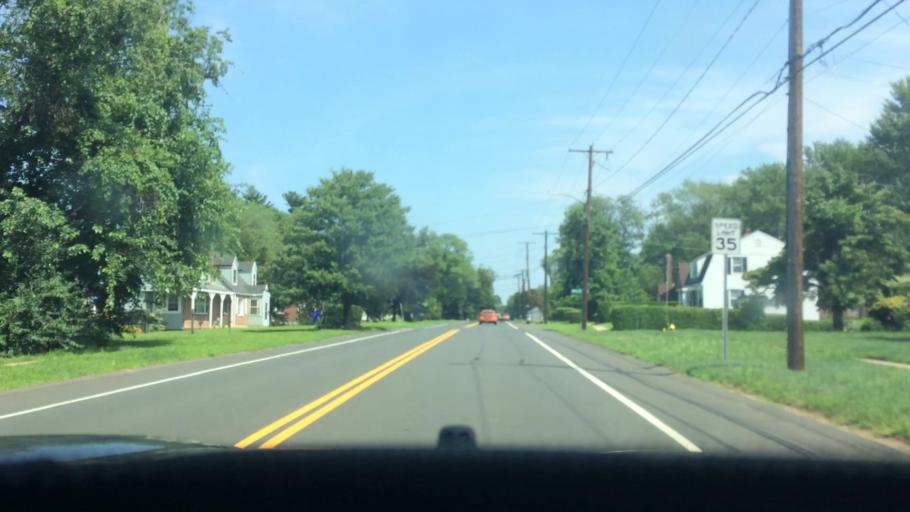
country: US
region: Connecticut
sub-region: Hartford County
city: Blue Hills
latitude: 41.8229
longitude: -72.7032
